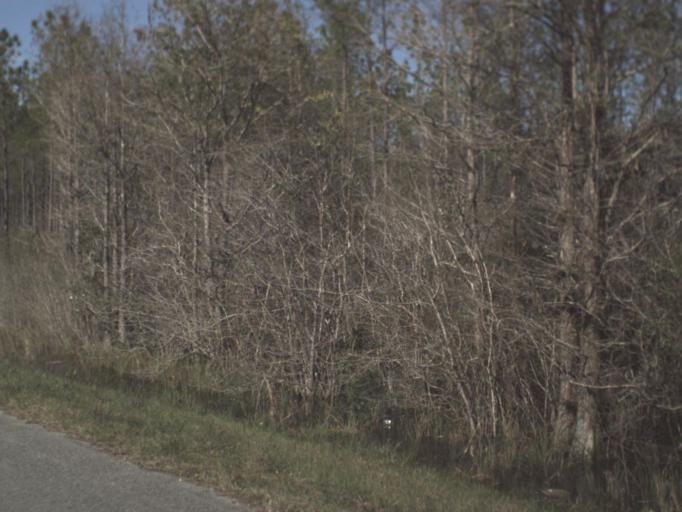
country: US
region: Florida
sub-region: Gulf County
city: Wewahitchka
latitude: 29.9952
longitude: -85.1709
